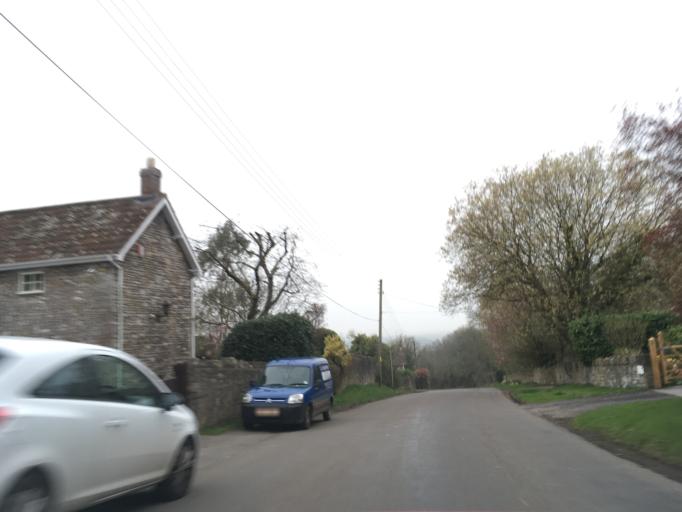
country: GB
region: England
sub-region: South Gloucestershire
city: Almondsbury
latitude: 51.5813
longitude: -2.5633
